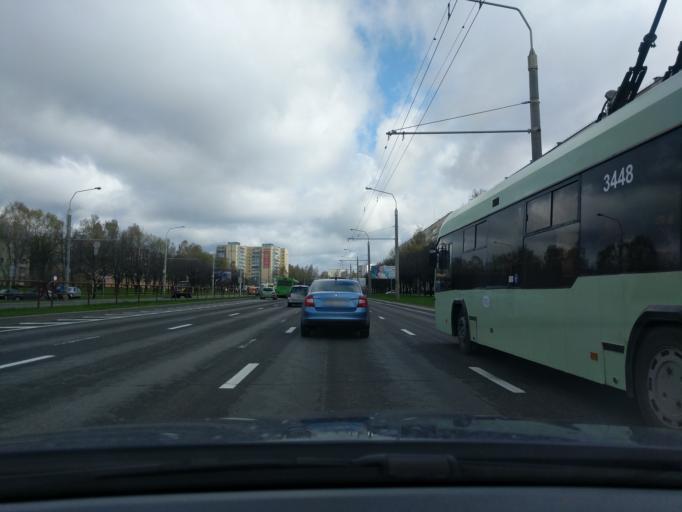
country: BY
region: Minsk
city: Novoye Medvezhino
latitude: 53.9127
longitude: 27.4953
